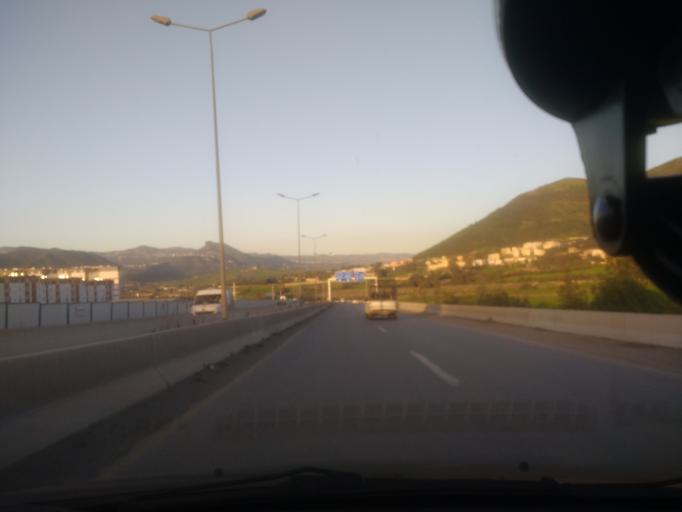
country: DZ
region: Boumerdes
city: Draa Ben Khedda
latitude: 36.7374
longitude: 4.0035
